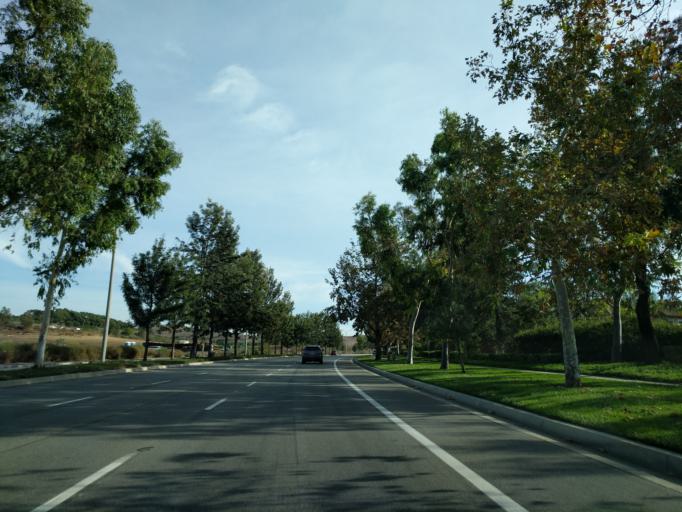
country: US
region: California
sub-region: Orange County
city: North Tustin
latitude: 33.7213
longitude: -117.7421
